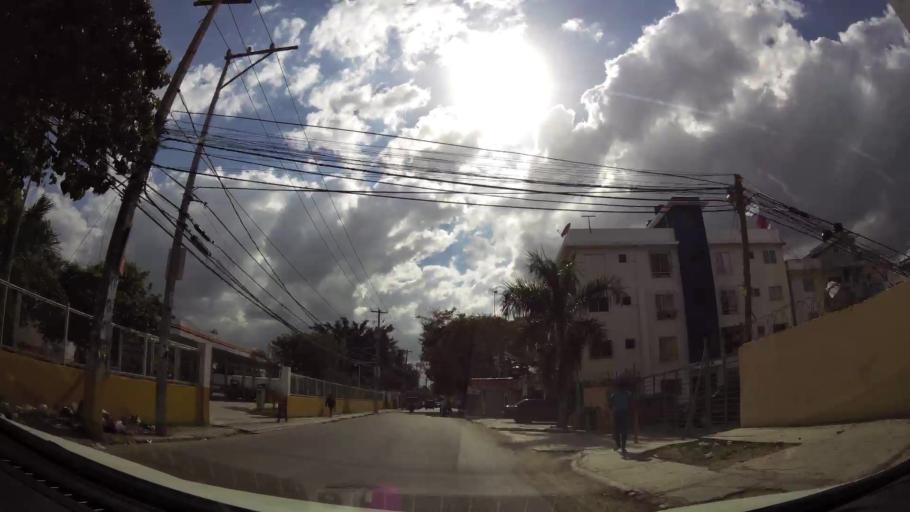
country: DO
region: Nacional
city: Ensanche Luperon
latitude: 18.5437
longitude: -69.8920
